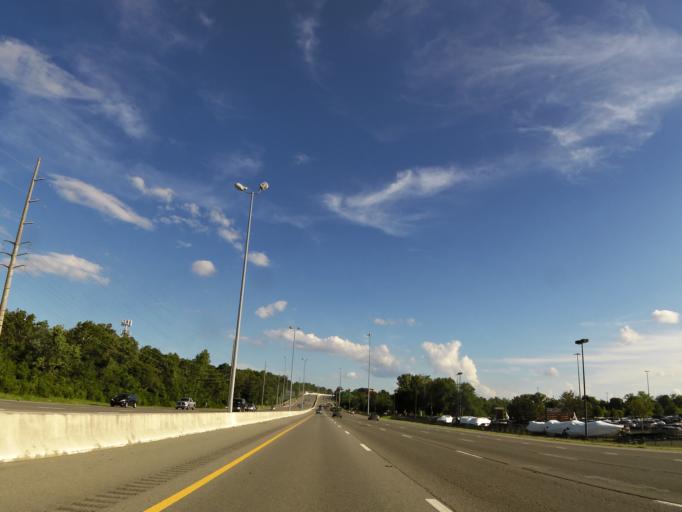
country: US
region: Tennessee
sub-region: Davidson County
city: Lakewood
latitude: 36.2022
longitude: -86.6893
